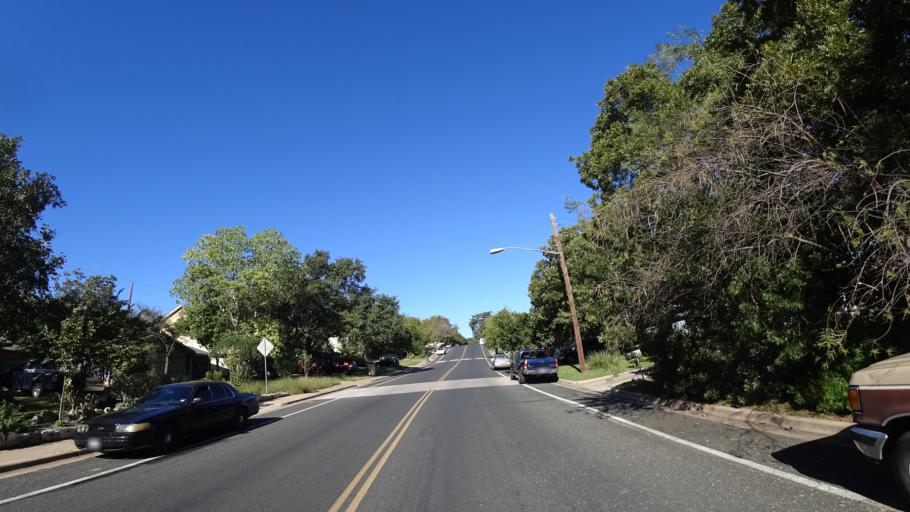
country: US
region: Texas
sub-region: Travis County
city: Austin
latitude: 30.2307
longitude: -97.7624
